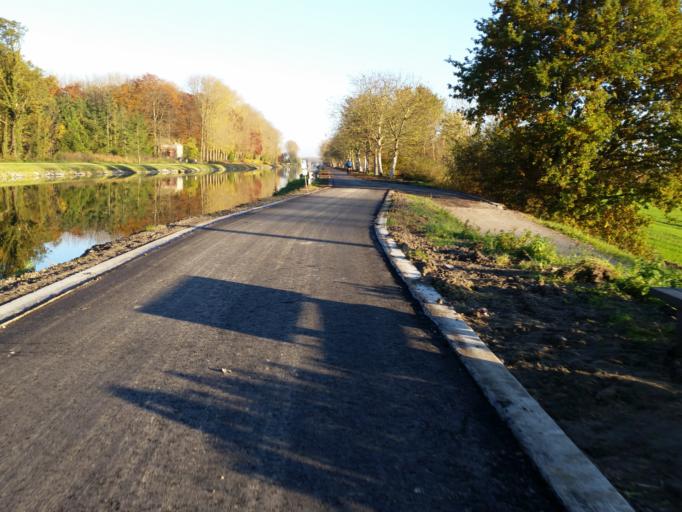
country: BE
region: Flanders
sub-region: Provincie Vlaams-Brabant
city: Haacht
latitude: 50.9509
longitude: 4.6227
